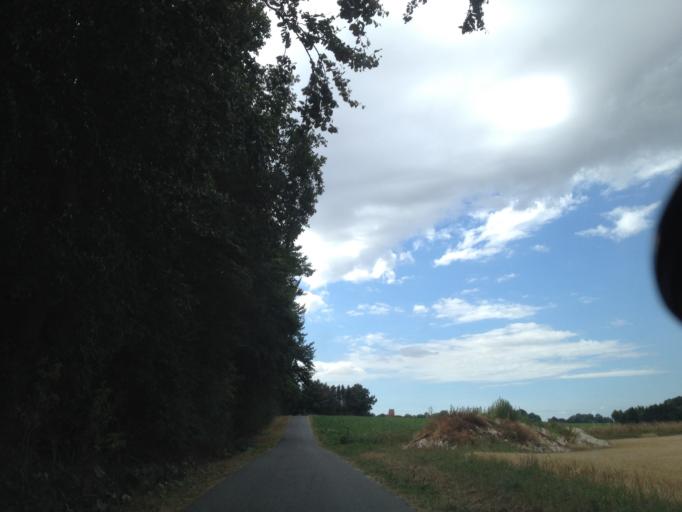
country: DK
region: Zealand
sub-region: Guldborgsund Kommune
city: Sakskobing
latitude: 54.7532
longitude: 11.6793
